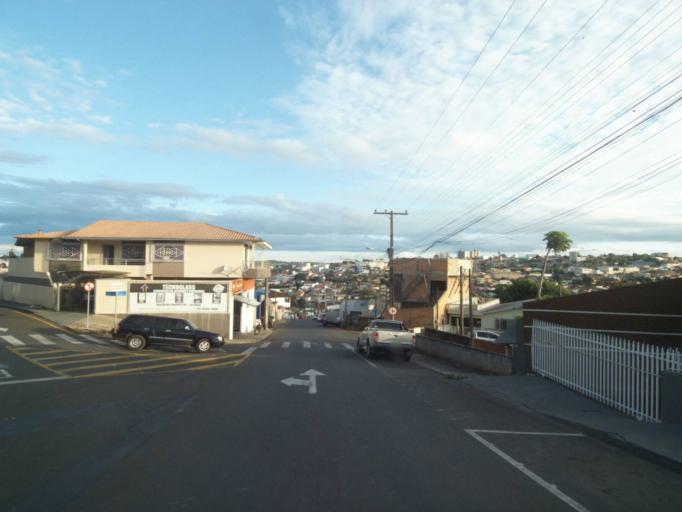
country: BR
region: Parana
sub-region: Telemaco Borba
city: Telemaco Borba
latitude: -24.3242
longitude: -50.6331
